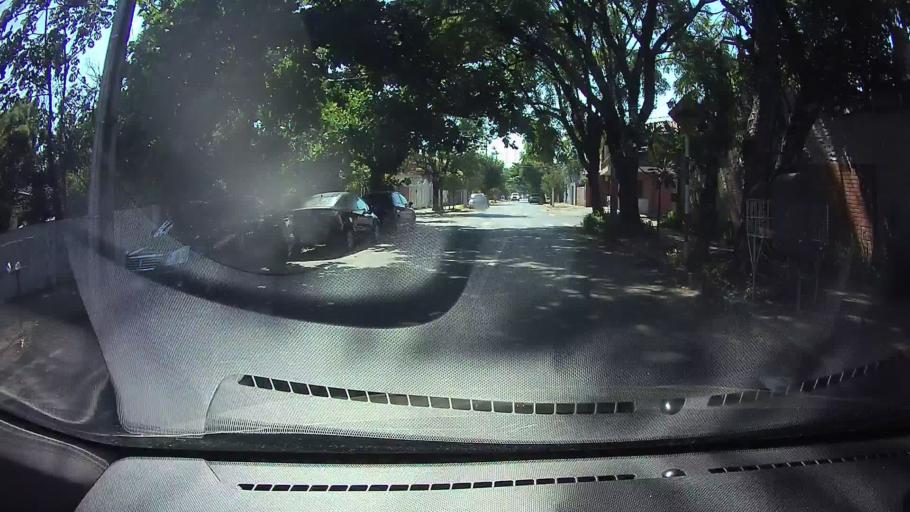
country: PY
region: Central
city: Fernando de la Mora
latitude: -25.2902
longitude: -57.5668
